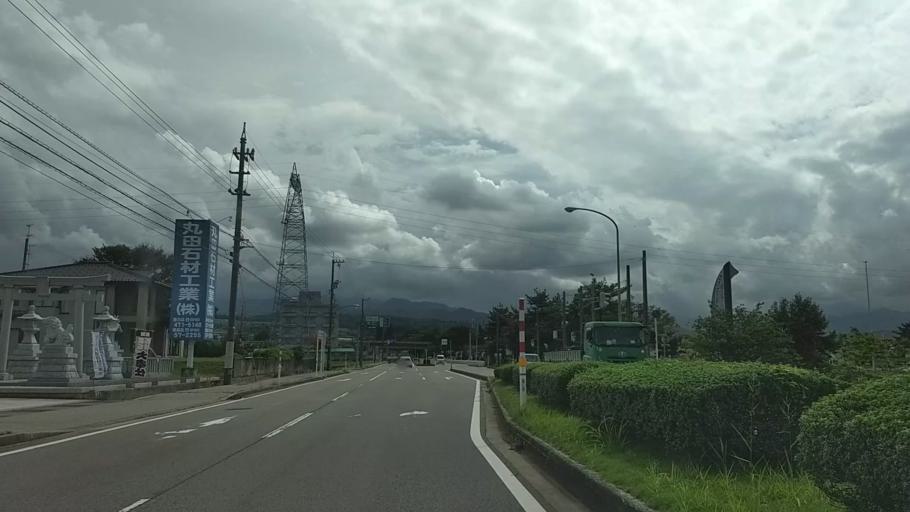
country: JP
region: Toyama
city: Kamiichi
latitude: 36.7455
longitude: 137.3778
